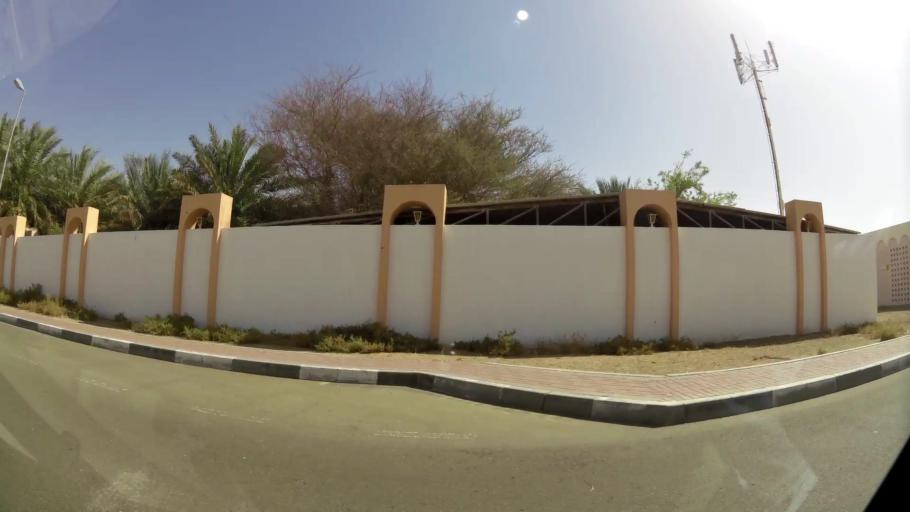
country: OM
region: Al Buraimi
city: Al Buraymi
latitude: 24.3017
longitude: 55.8011
